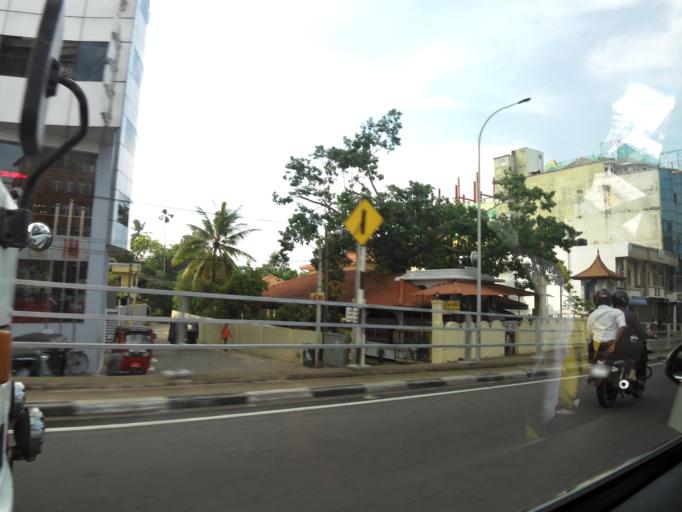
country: LK
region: Western
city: Kolonnawa
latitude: 6.9385
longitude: 79.8783
